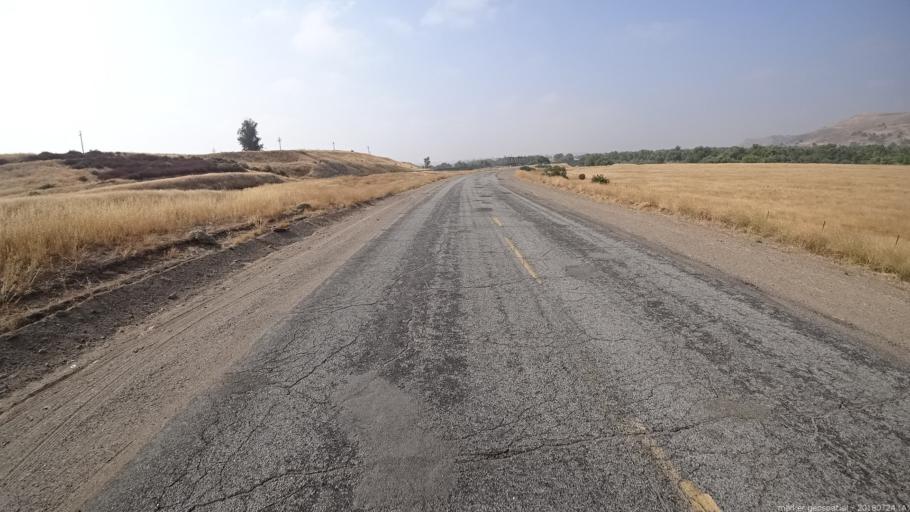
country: US
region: California
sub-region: San Luis Obispo County
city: San Miguel
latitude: 35.8296
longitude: -120.7500
